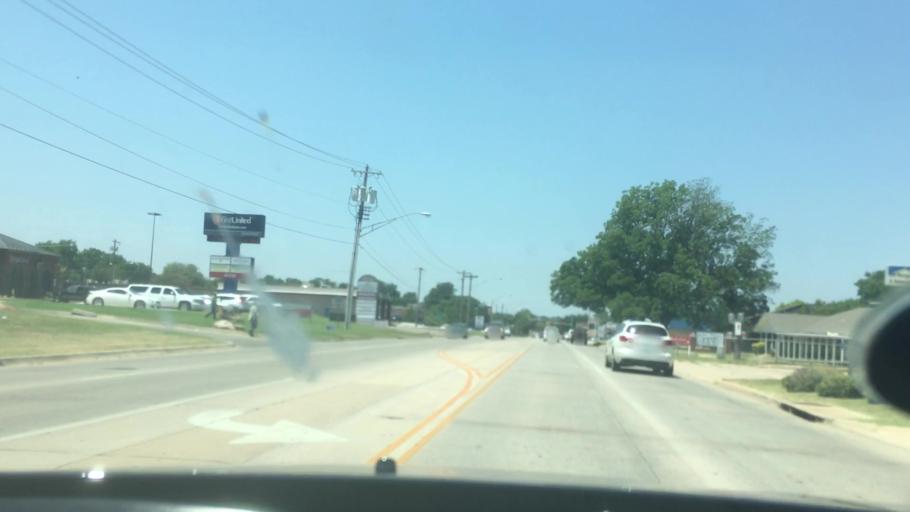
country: US
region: Oklahoma
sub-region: Pontotoc County
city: Ada
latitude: 34.7817
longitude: -96.6600
